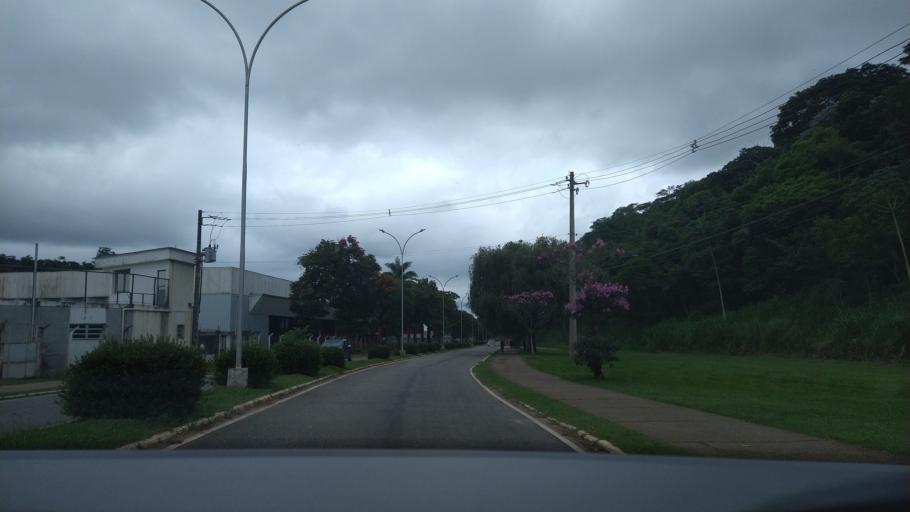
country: BR
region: Minas Gerais
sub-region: Vicosa
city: Vicosa
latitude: -20.7665
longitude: -42.8620
